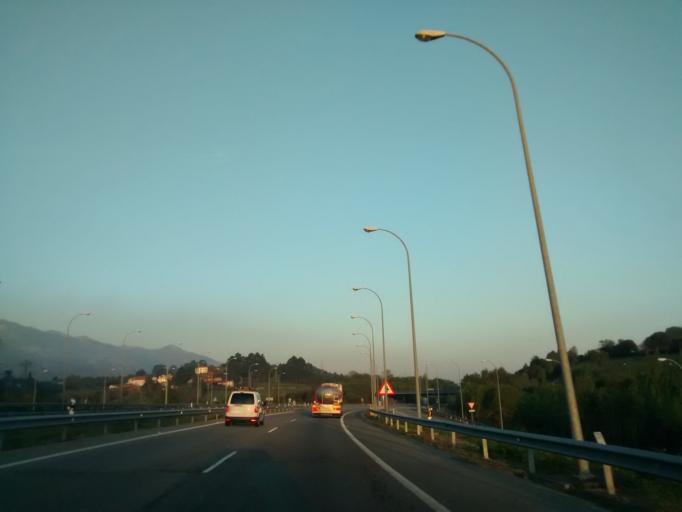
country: ES
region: Asturias
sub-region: Province of Asturias
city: Colunga
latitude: 43.4692
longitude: -5.1717
